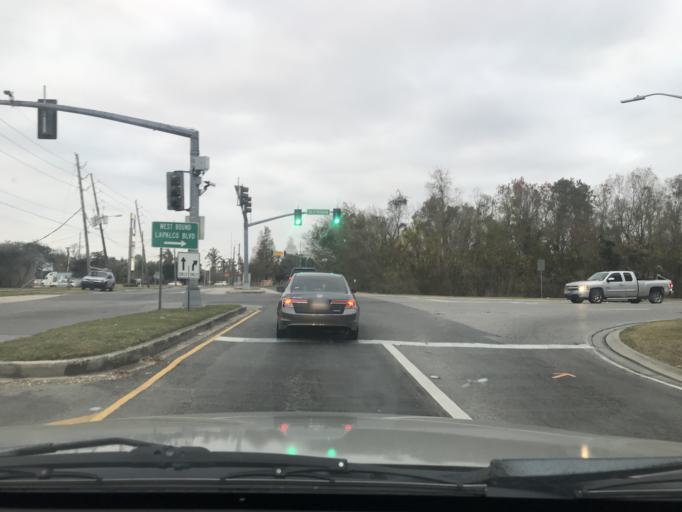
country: US
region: Louisiana
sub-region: Jefferson Parish
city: Woodmere
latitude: 29.8683
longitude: -90.0752
